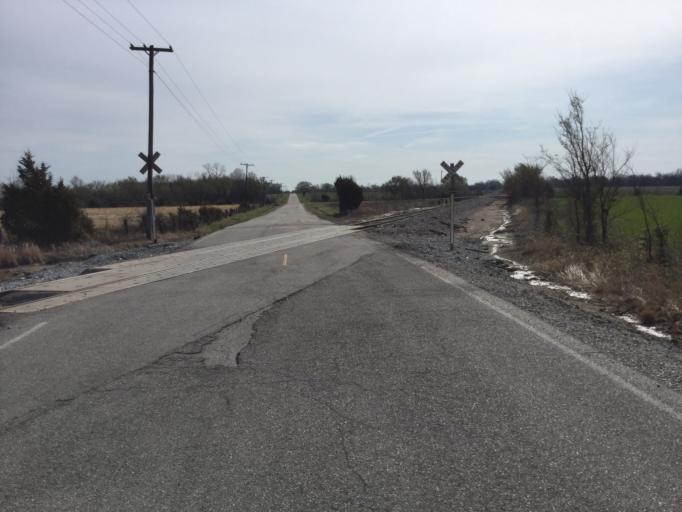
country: US
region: Kansas
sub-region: Cherokee County
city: Galena
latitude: 37.1192
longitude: -94.7252
